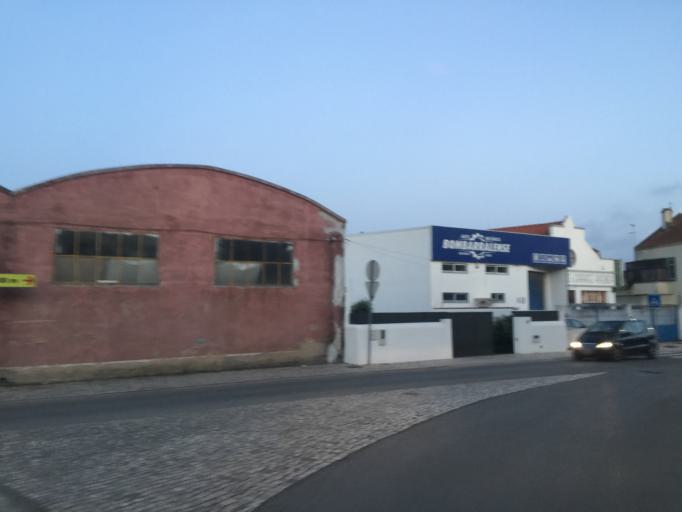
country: PT
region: Leiria
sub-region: Bombarral
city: Bombarral
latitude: 39.2664
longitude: -9.1548
